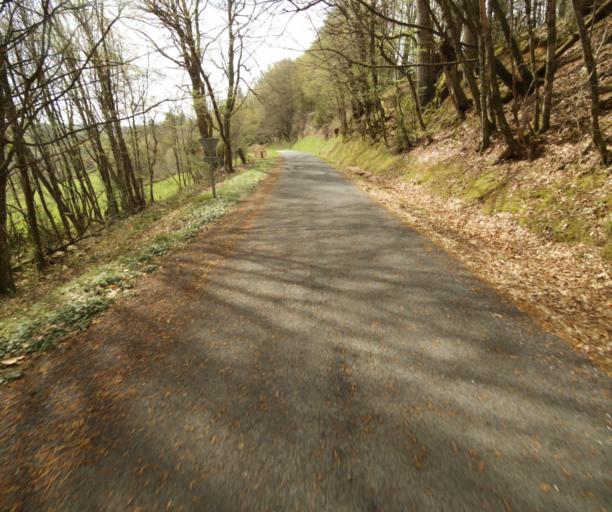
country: FR
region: Limousin
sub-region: Departement de la Correze
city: Laguenne
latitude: 45.2574
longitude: 1.8164
